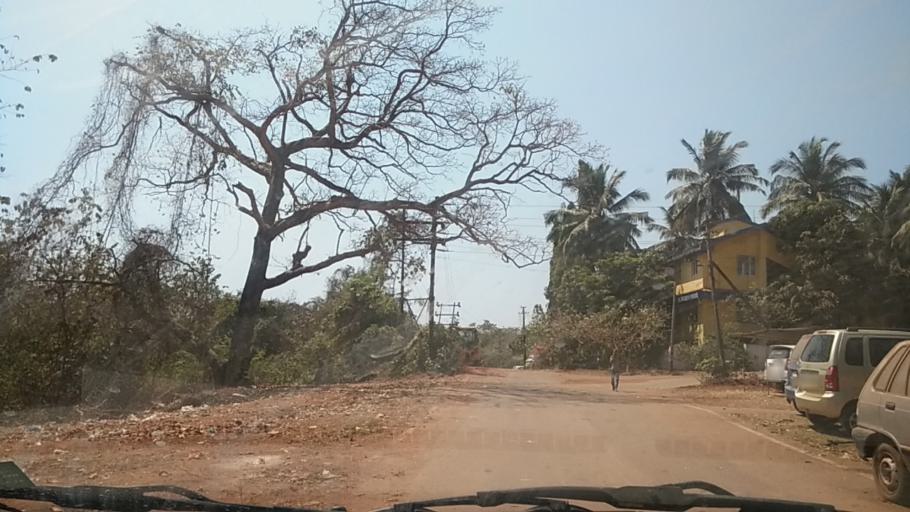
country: IN
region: Goa
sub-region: North Goa
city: Panaji
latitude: 15.5140
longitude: 73.8387
